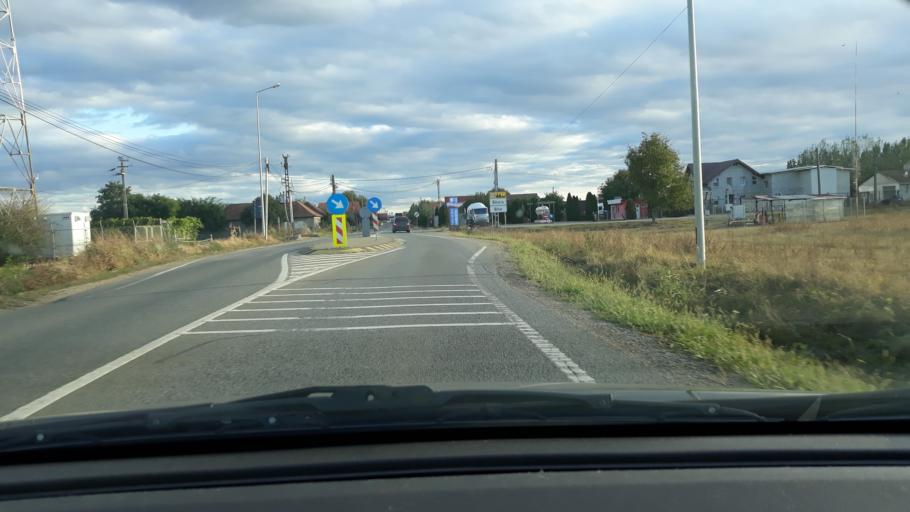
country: RO
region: Bihor
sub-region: Comuna Biharea
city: Biharea
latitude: 47.1708
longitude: 21.9218
